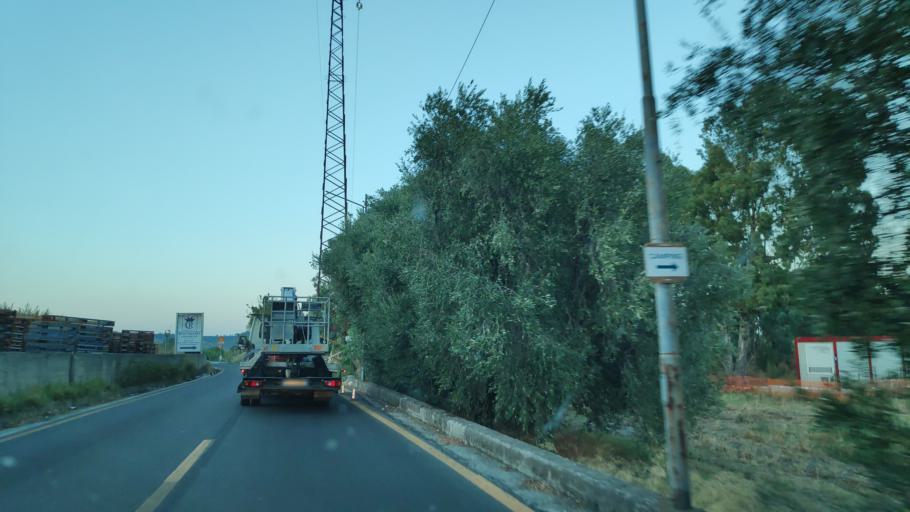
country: IT
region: Calabria
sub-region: Provincia di Reggio Calabria
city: Caulonia Marina
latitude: 38.3480
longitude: 16.4696
